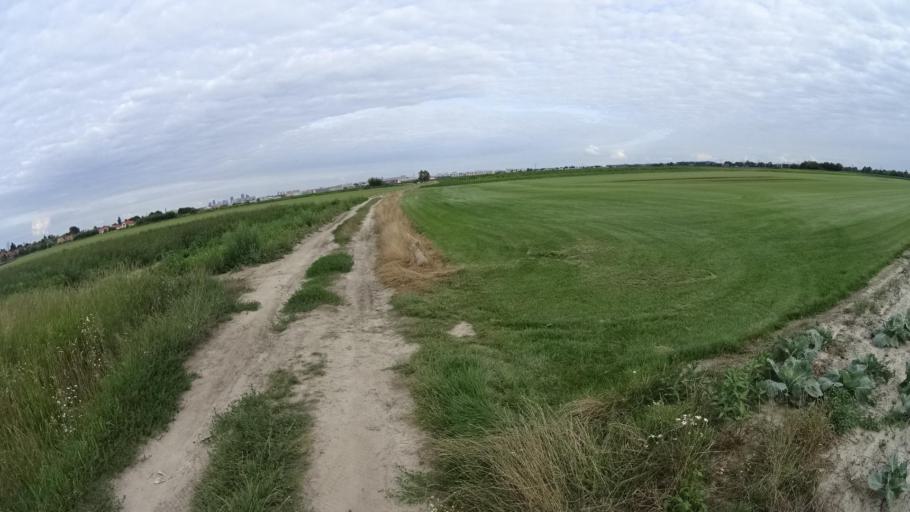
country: PL
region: Masovian Voivodeship
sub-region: Powiat warszawski zachodni
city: Babice
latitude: 52.2398
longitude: 20.8634
